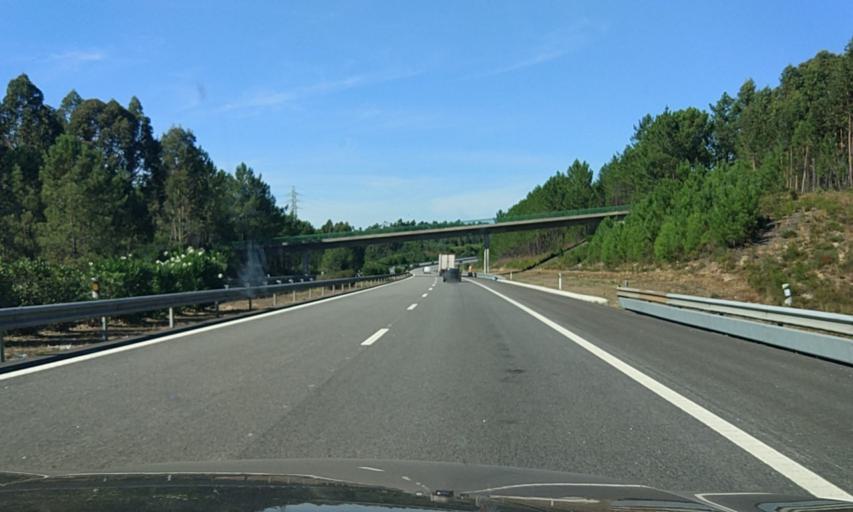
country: PT
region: Leiria
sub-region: Leiria
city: Caranguejeira
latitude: 39.8437
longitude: -8.7103
